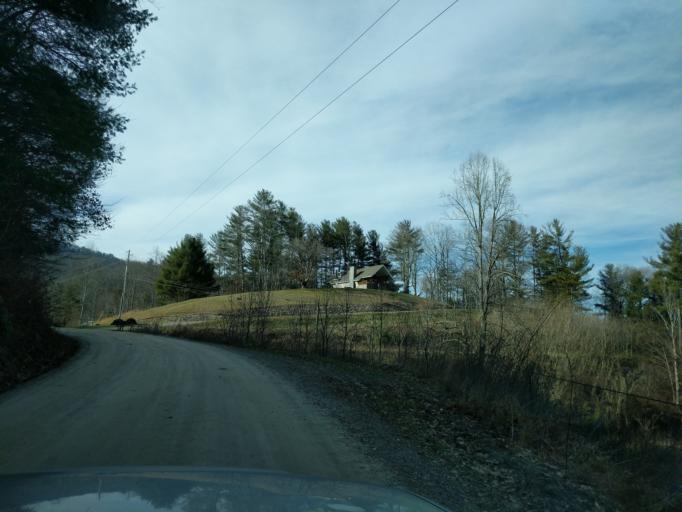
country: US
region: North Carolina
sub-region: Haywood County
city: Cove Creek
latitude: 35.6724
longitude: -83.0329
